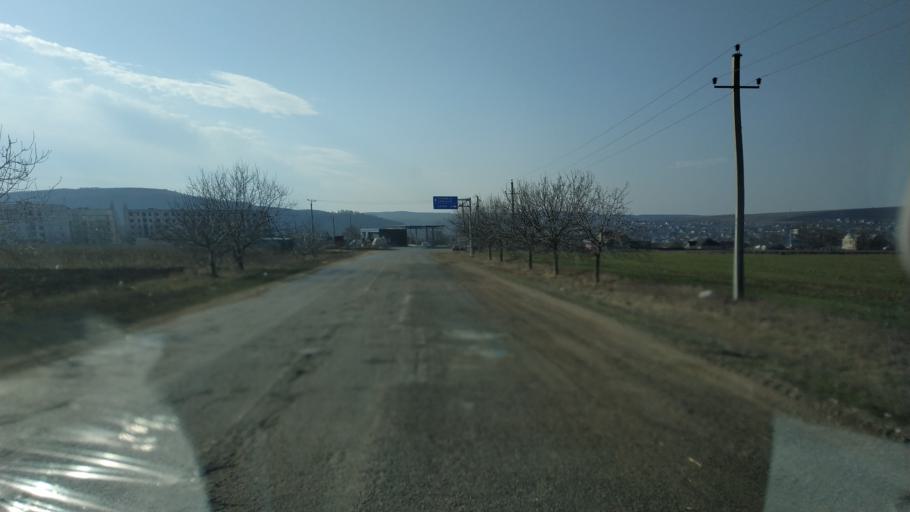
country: MD
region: Chisinau
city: Singera
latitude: 46.6898
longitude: 29.0532
